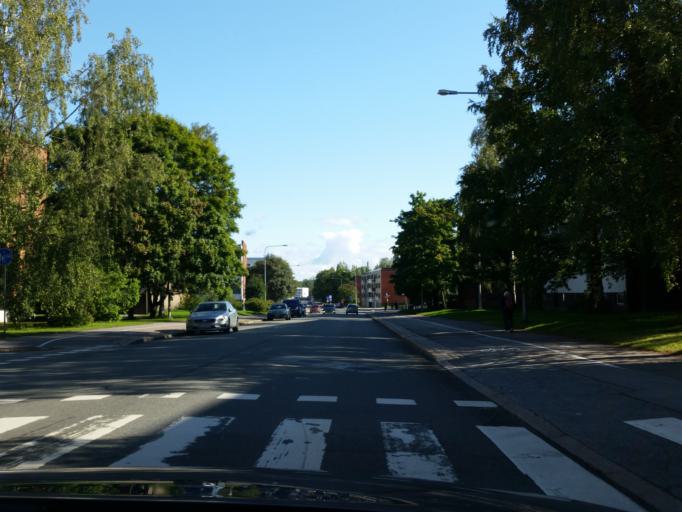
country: FI
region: Uusimaa
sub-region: Helsinki
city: Helsinki
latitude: 60.2235
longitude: 24.9497
